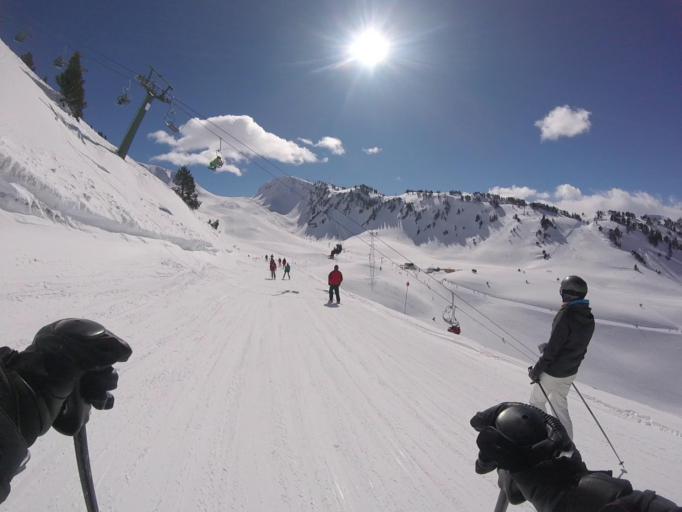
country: ES
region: Catalonia
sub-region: Provincia de Lleida
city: Espot
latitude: 42.6859
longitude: 0.9648
